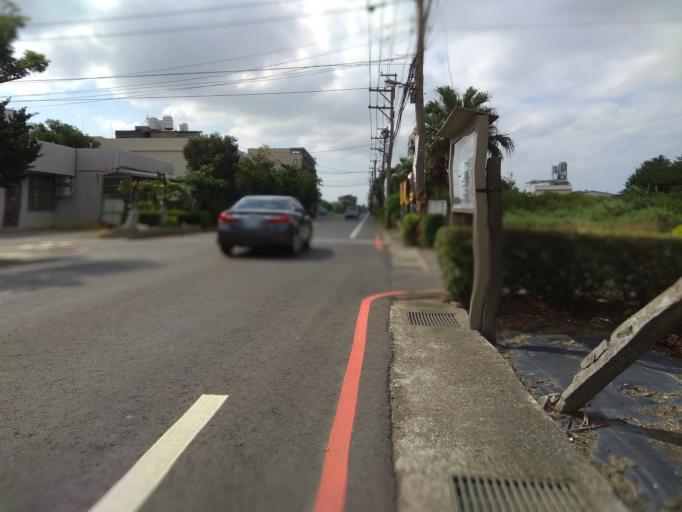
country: TW
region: Taiwan
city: Taoyuan City
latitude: 25.0634
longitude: 121.2376
